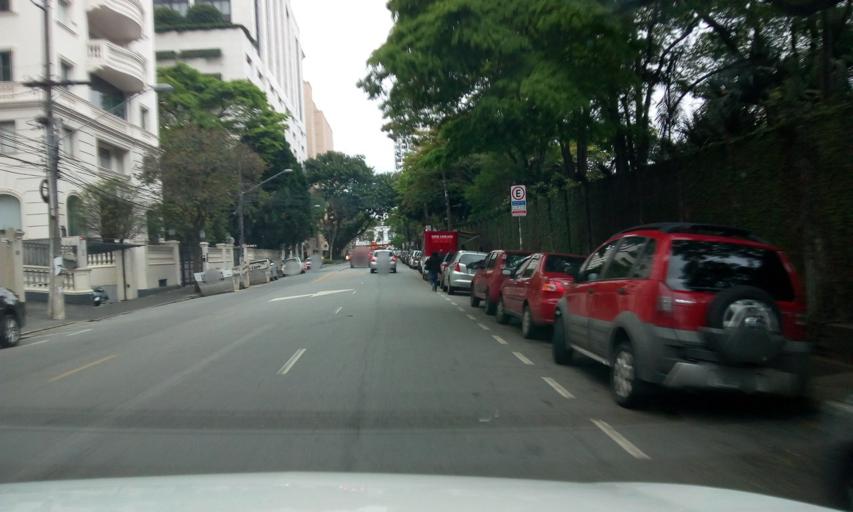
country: BR
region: Sao Paulo
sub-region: Sao Paulo
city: Sao Paulo
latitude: -23.5790
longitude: -46.6897
